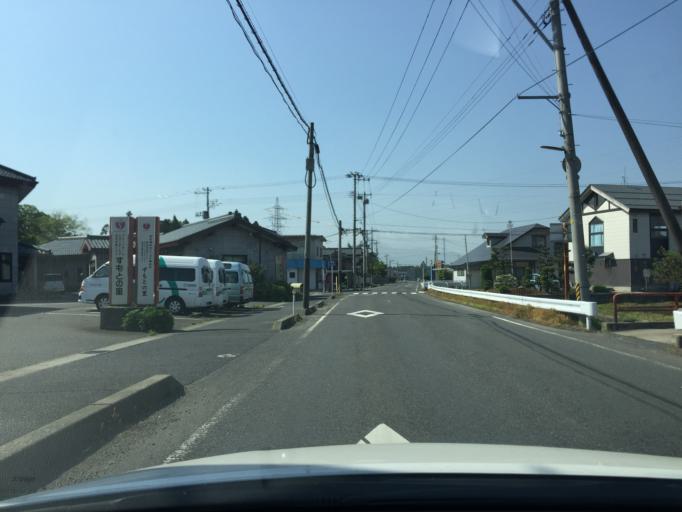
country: JP
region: Niigata
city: Gosen
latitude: 37.7473
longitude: 139.2037
